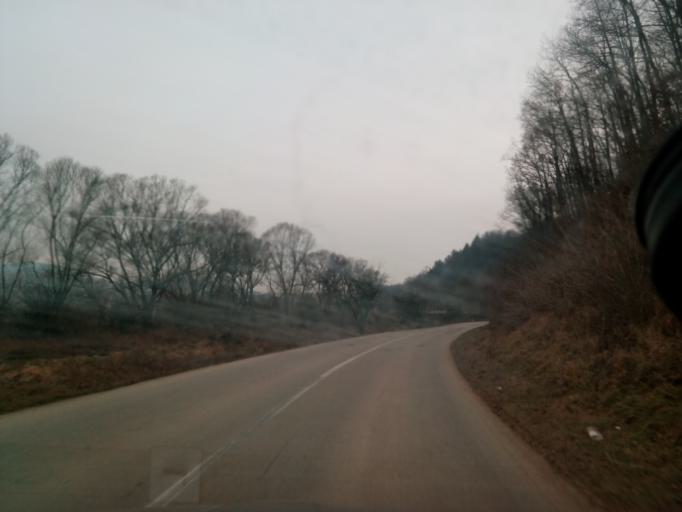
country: SK
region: Kosicky
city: Medzev
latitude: 48.6964
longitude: 20.9164
